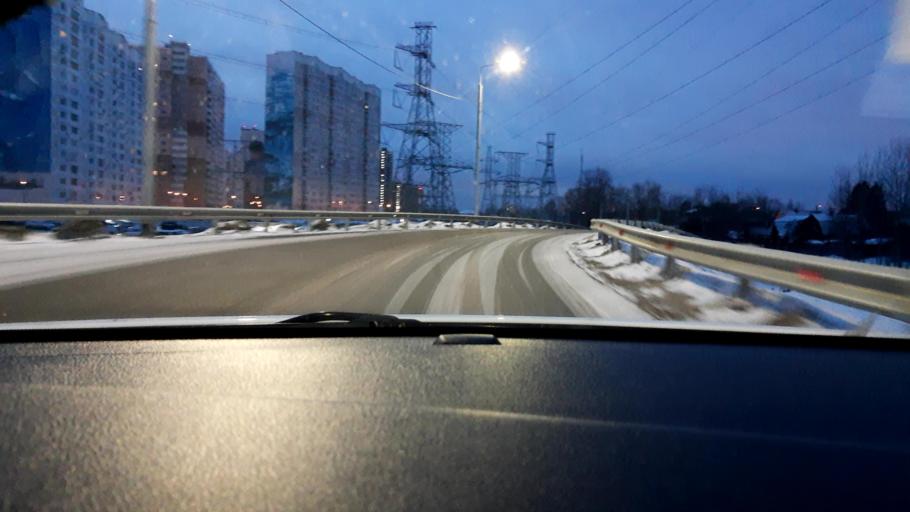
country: RU
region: Moskovskaya
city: Nemchinovka
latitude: 55.7082
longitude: 37.3179
